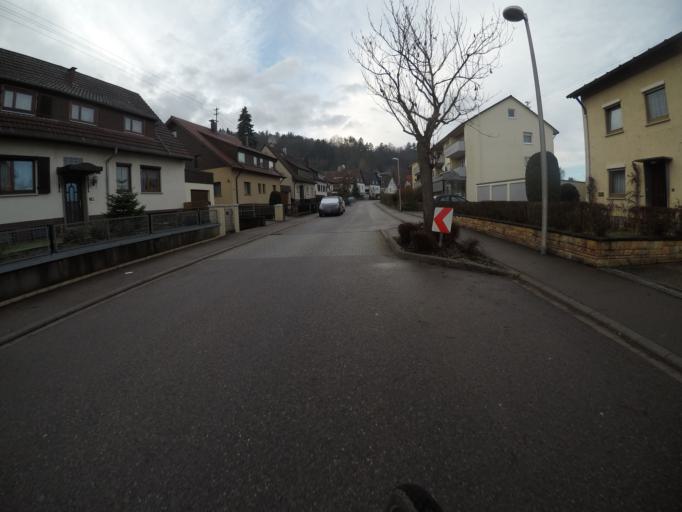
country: DE
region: Baden-Wuerttemberg
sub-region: Regierungsbezirk Stuttgart
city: Aidlingen
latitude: 48.6777
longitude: 8.9058
